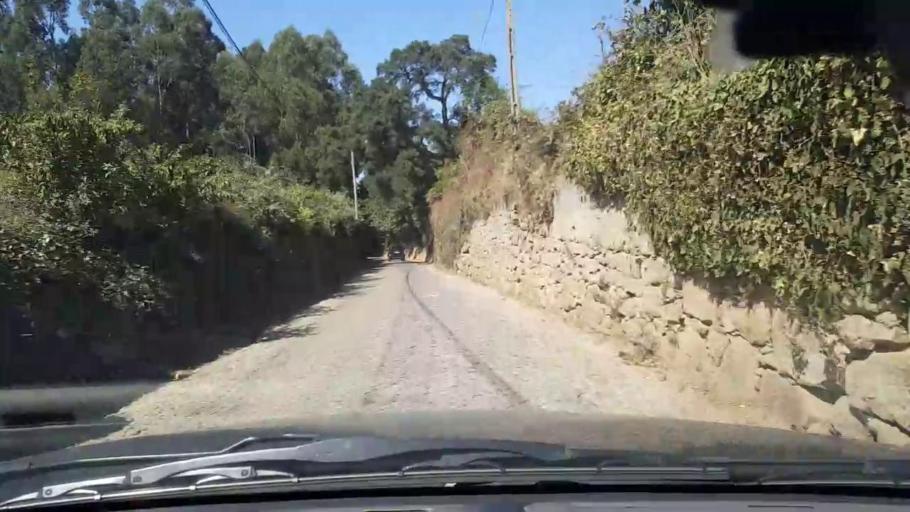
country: PT
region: Porto
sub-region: Matosinhos
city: Lavra
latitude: 41.2728
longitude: -8.6945
